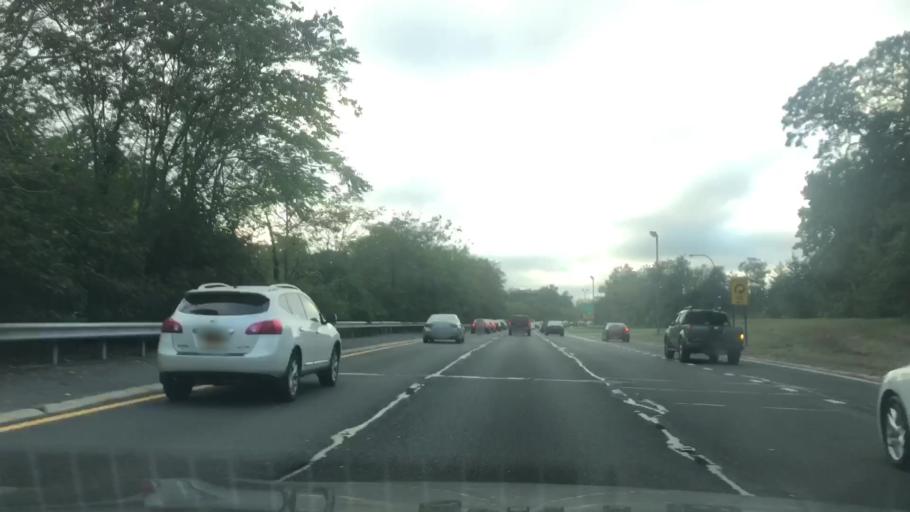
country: US
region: New York
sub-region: Nassau County
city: North Merrick
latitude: 40.6908
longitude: -73.5779
